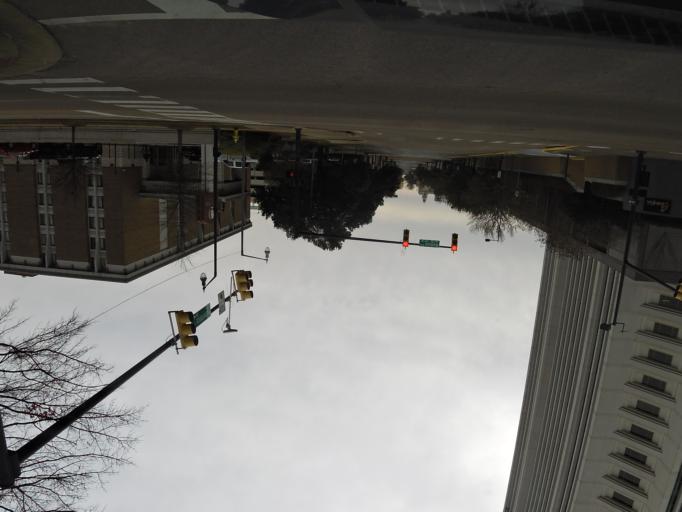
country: US
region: Alabama
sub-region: Montgomery County
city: Montgomery
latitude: 32.3802
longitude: -86.3062
